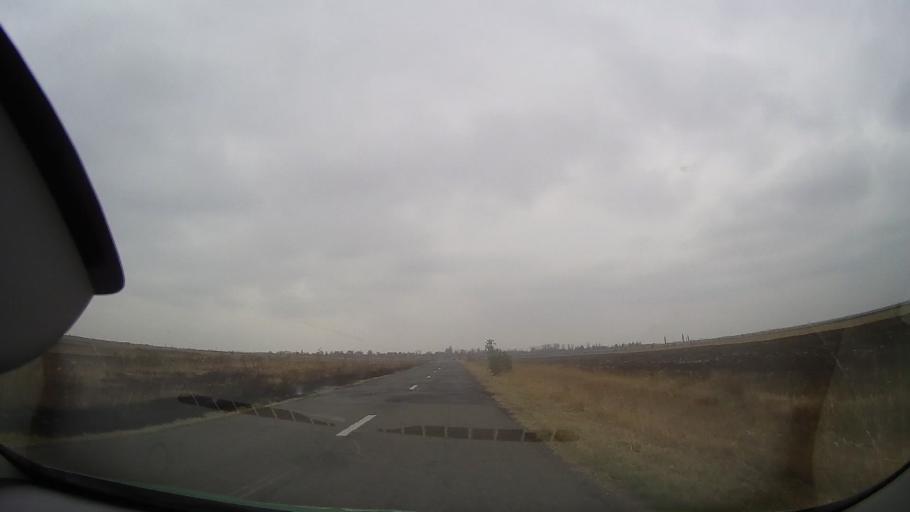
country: RO
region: Ialomita
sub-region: Comuna Garbovi
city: Garbovi
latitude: 44.7641
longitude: 26.7953
